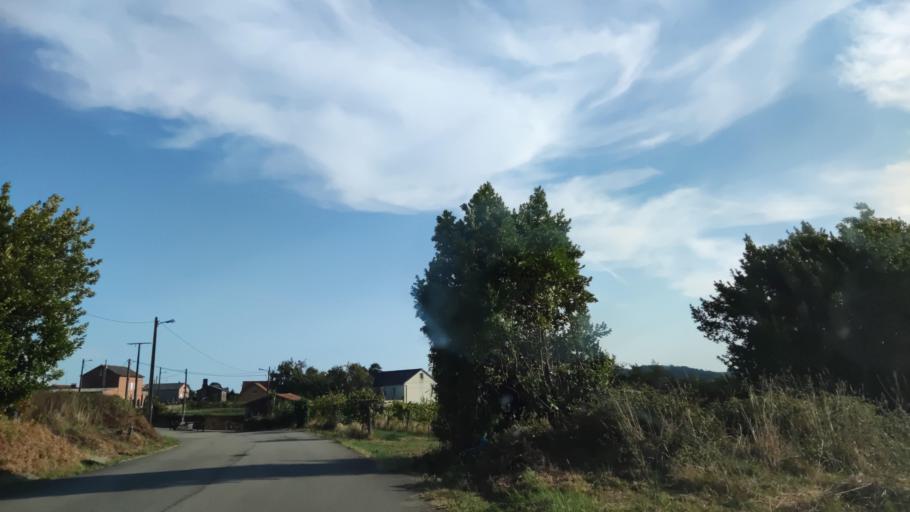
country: ES
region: Galicia
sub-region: Provincia da Coruna
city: Rianxo
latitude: 42.6960
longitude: -8.8475
